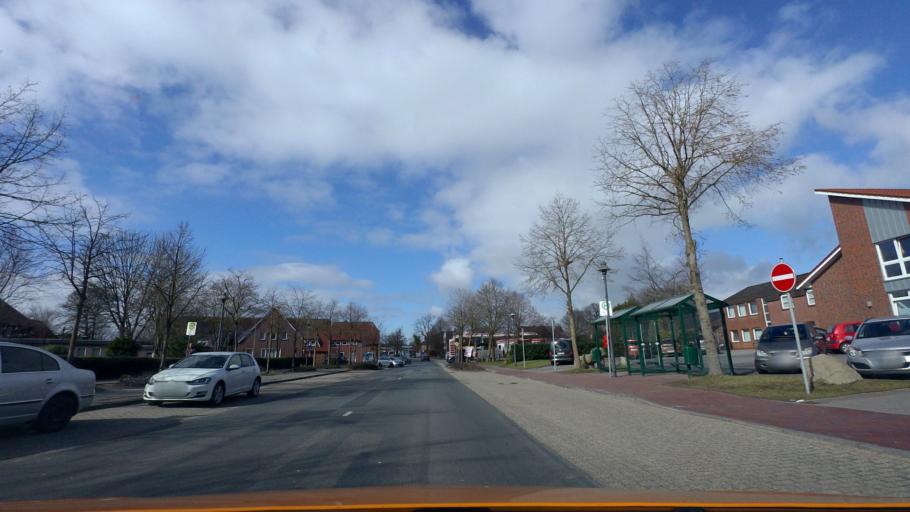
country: DE
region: Lower Saxony
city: Bosel
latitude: 53.0058
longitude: 7.9548
